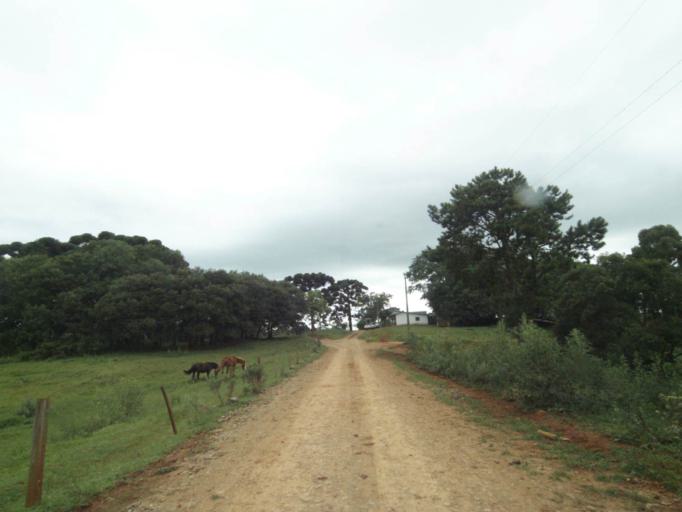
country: BR
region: Rio Grande do Sul
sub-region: Lagoa Vermelha
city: Lagoa Vermelha
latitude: -28.1971
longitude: -51.5388
